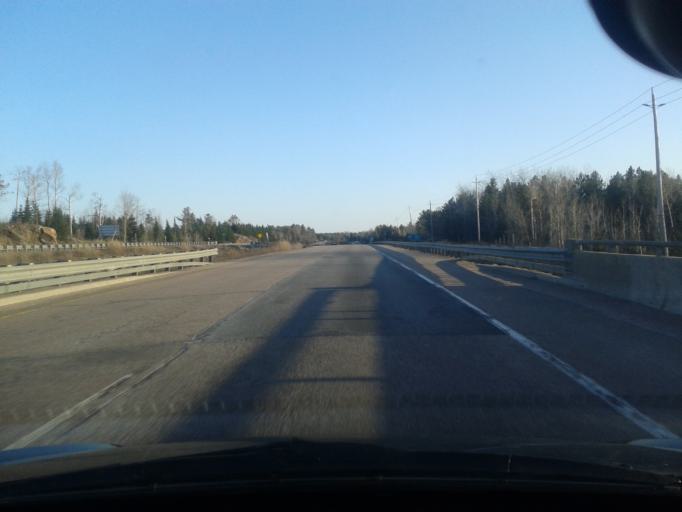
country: CA
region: Ontario
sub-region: Nipissing District
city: North Bay
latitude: 46.2240
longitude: -79.3504
